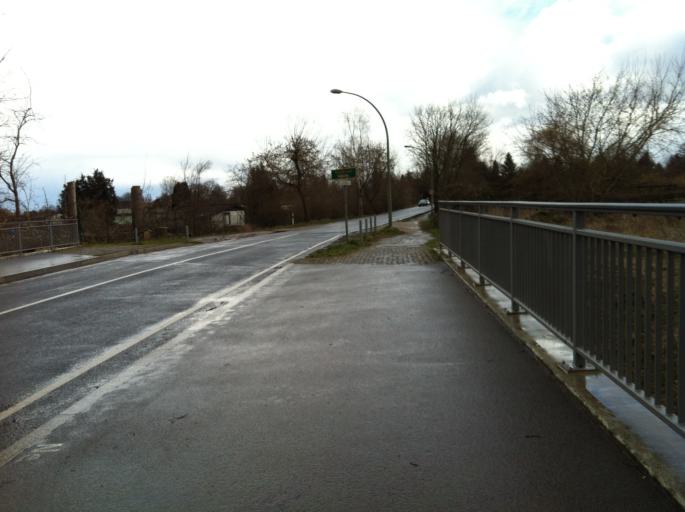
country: DE
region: Berlin
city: Karow
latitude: 52.6164
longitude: 13.4597
